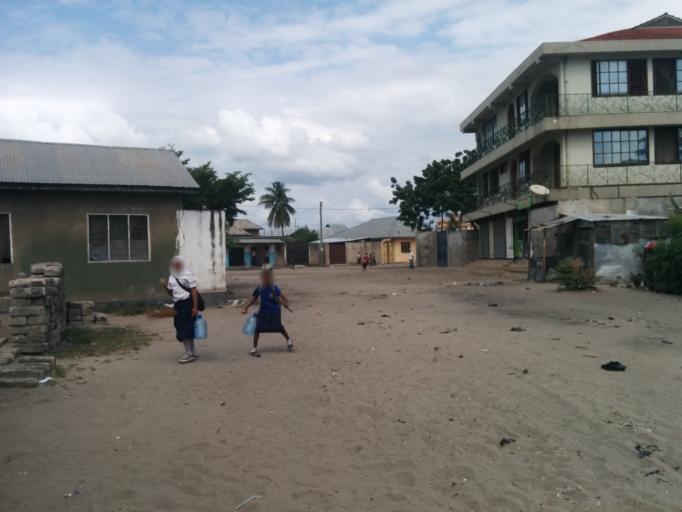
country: TZ
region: Dar es Salaam
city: Dar es Salaam
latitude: -6.8654
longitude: 39.2547
